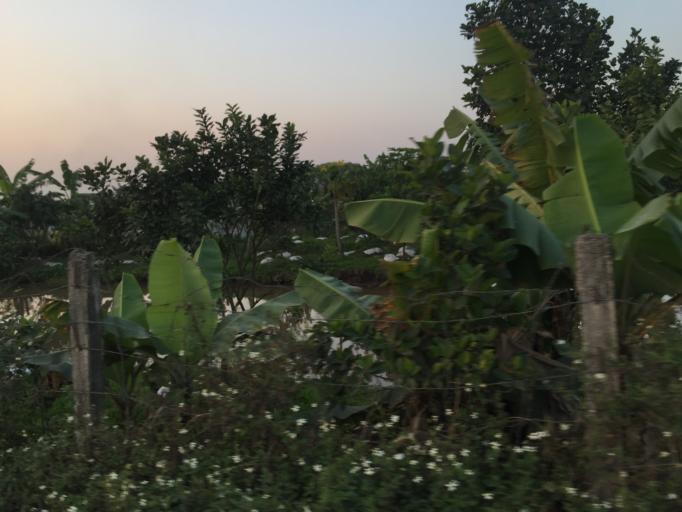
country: VN
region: Ha Noi
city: Chuc Son
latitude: 20.8923
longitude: 105.7215
